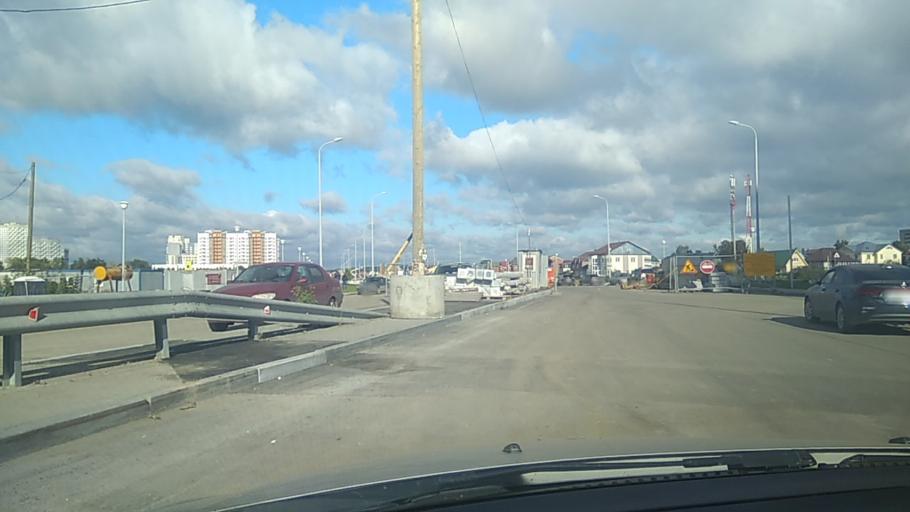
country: RU
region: Sverdlovsk
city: Shirokaya Rechka
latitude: 56.7990
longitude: 60.5112
